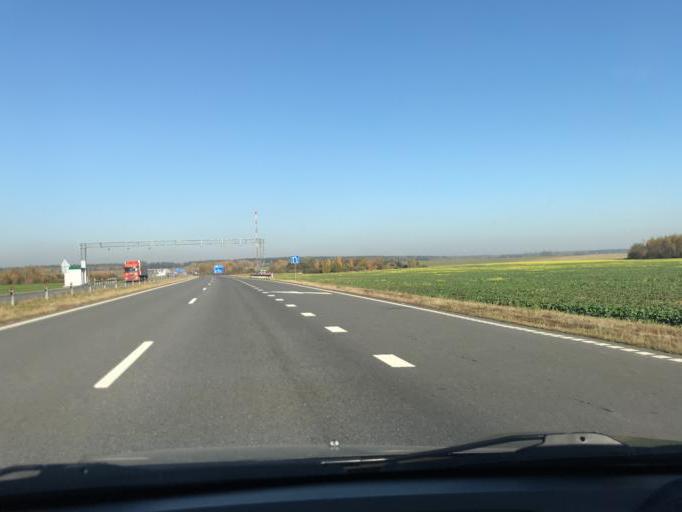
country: BY
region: Mogilev
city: Babruysk
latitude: 53.1738
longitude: 29.3601
